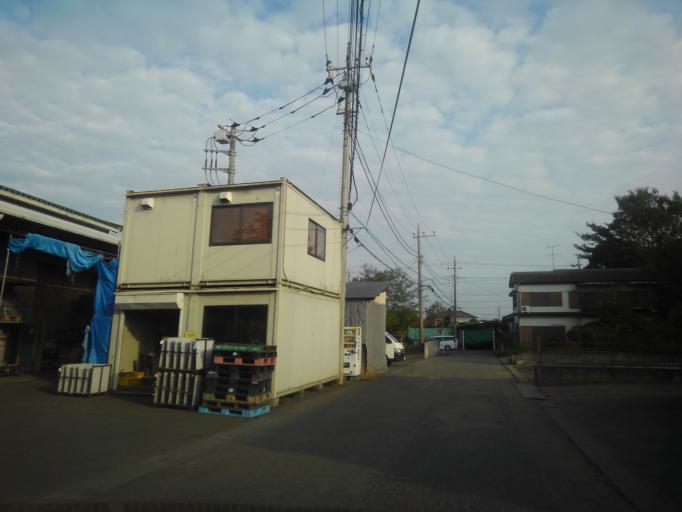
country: JP
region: Saitama
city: Sayama
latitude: 35.7901
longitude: 139.3771
